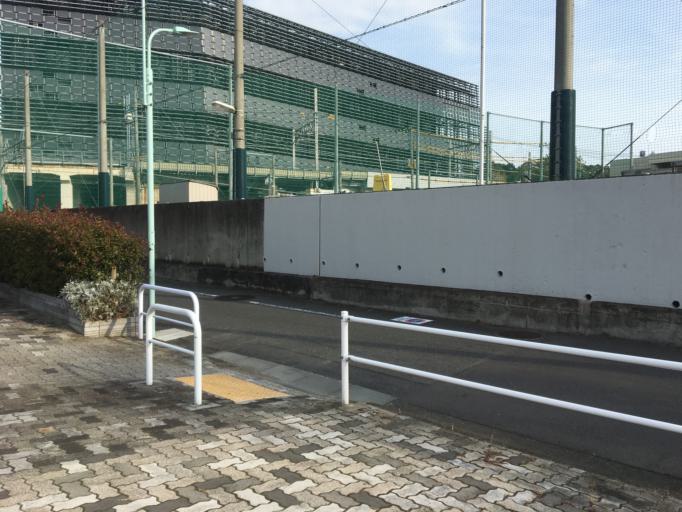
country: JP
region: Tokyo
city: Tokyo
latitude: 35.6055
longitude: 139.6804
